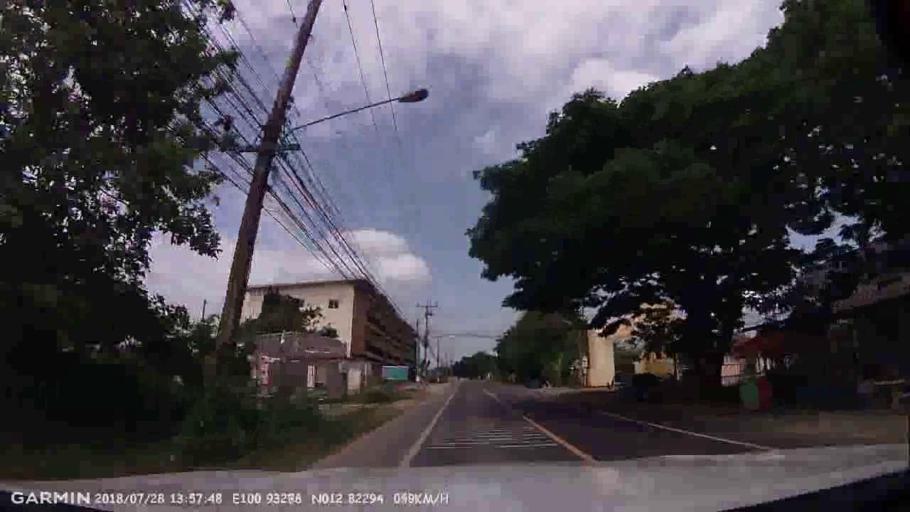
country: TH
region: Chon Buri
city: Phatthaya
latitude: 12.8230
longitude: 100.9328
